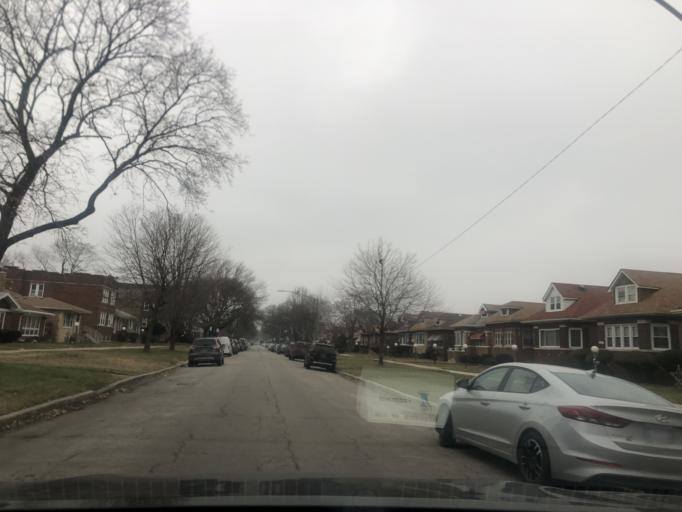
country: US
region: Illinois
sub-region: Cook County
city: Evergreen Park
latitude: 41.7476
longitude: -87.6214
